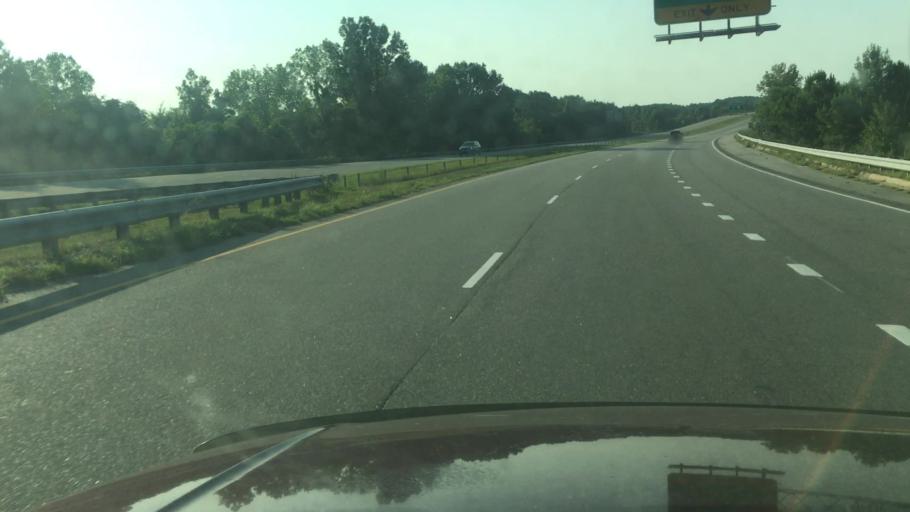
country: US
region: North Carolina
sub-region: Cumberland County
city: Fayetteville
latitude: 35.0372
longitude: -78.8833
